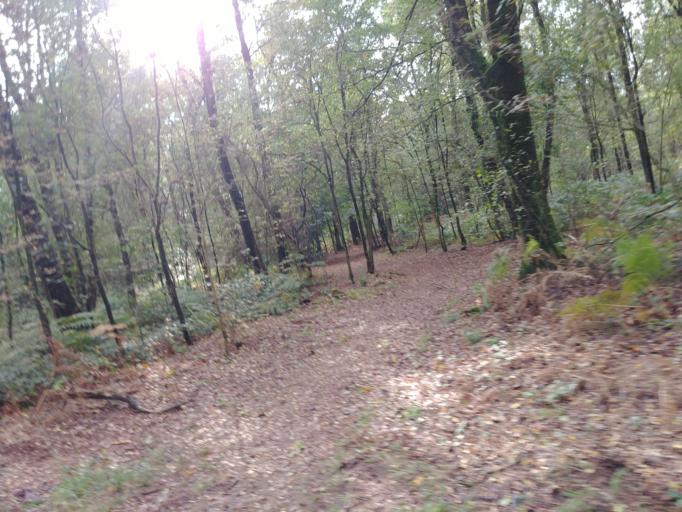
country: NL
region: Gelderland
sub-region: Gemeente Renkum
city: Doorwerth
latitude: 51.9815
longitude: 5.7900
